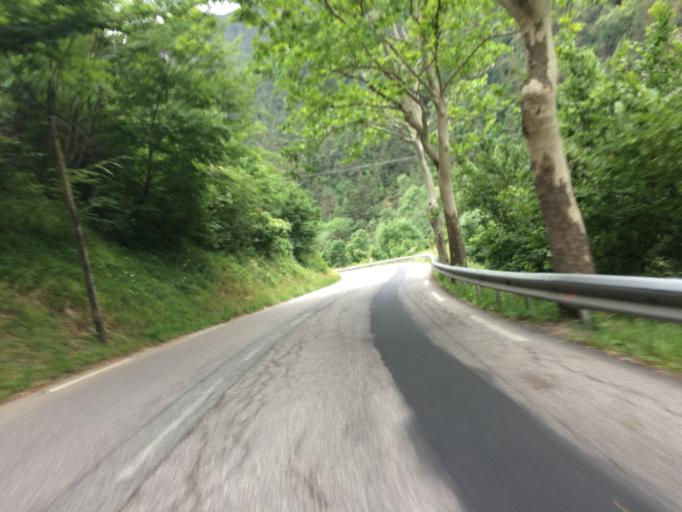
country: FR
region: Provence-Alpes-Cote d'Azur
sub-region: Departement des Alpes-Maritimes
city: Tende
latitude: 44.1039
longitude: 7.5745
